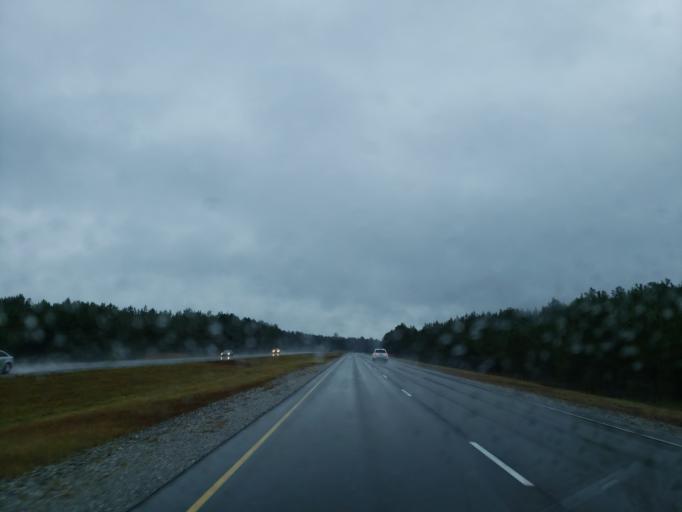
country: US
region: Mississippi
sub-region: Clarke County
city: Stonewall
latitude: 32.1442
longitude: -88.7142
